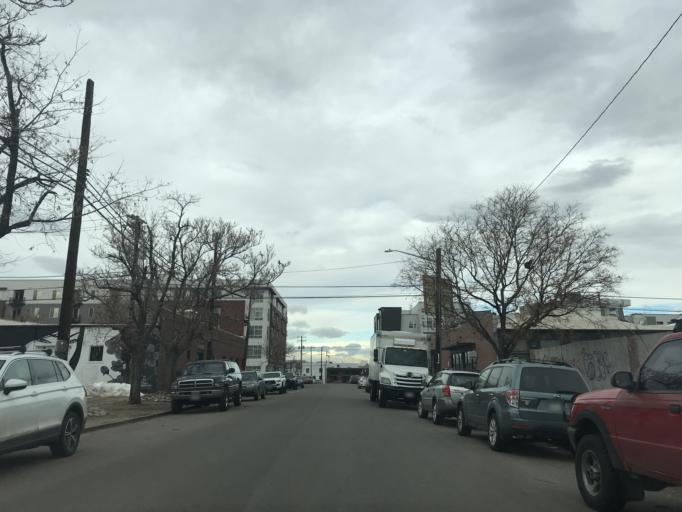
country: US
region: Colorado
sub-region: Denver County
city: Denver
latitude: 39.7604
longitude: -104.9829
